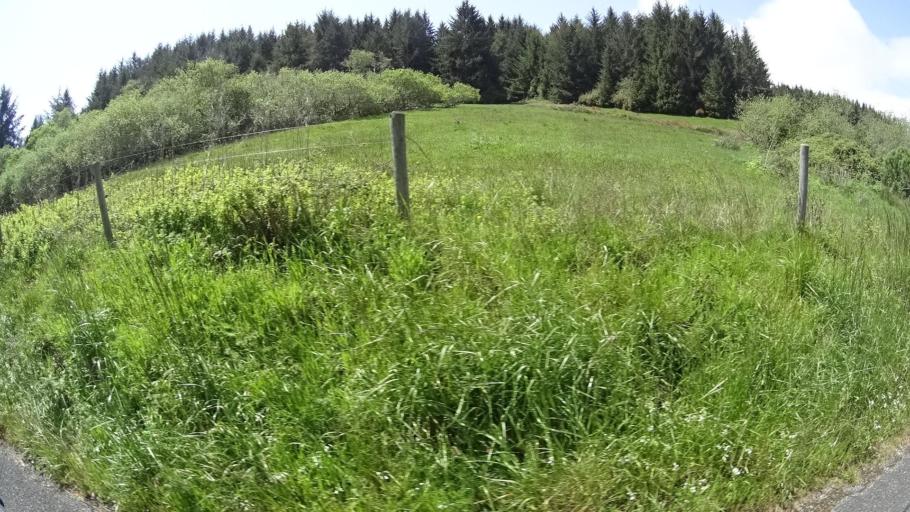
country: US
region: California
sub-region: Humboldt County
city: Humboldt Hill
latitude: 40.6711
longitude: -124.2111
